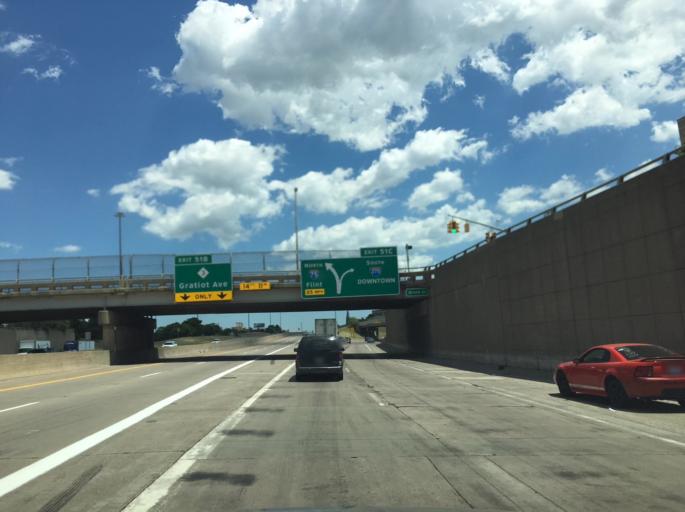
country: US
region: Michigan
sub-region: Wayne County
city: Detroit
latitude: 42.3414
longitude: -83.0491
